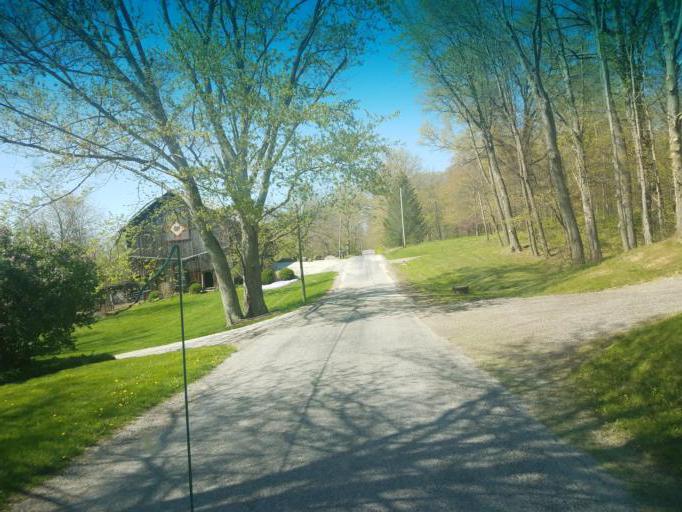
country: US
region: Ohio
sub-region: Medina County
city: Lodi
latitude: 40.9667
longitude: -82.0249
